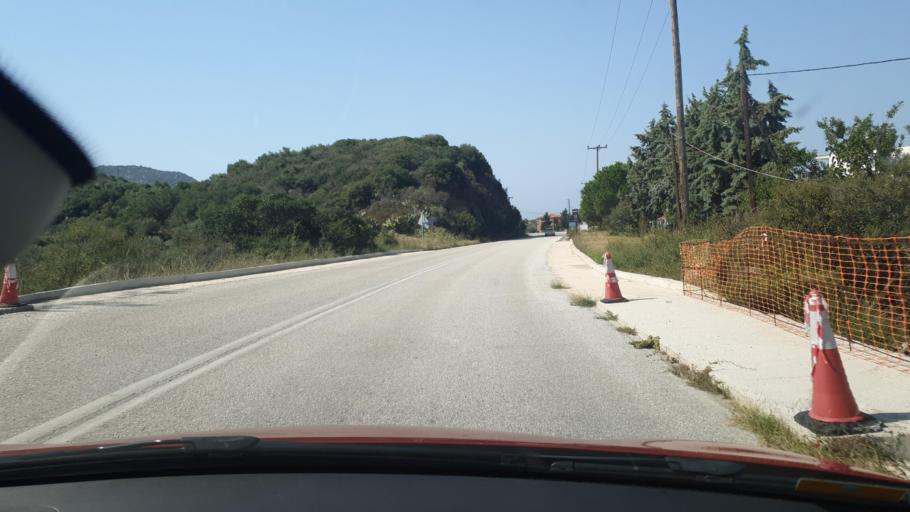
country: GR
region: Central Macedonia
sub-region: Nomos Chalkidikis
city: Sykia
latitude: 39.9862
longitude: 23.9119
